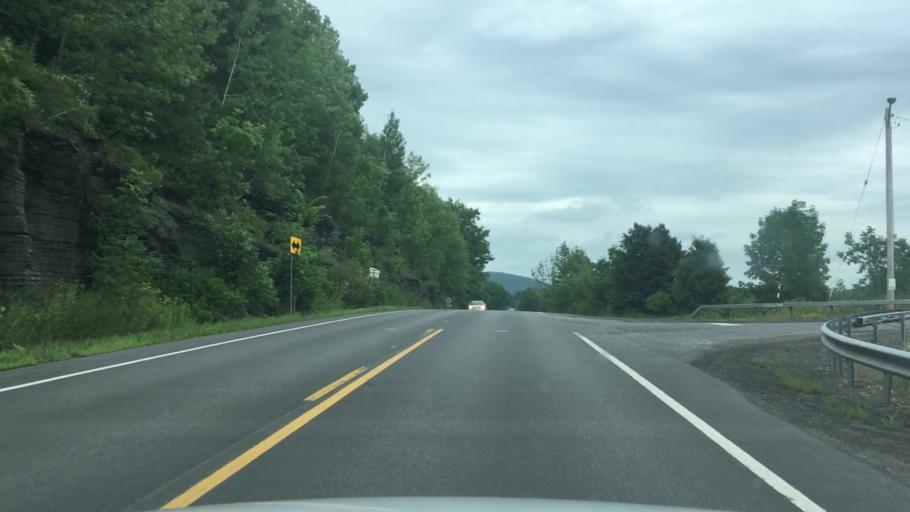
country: US
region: New York
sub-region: Otsego County
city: West End
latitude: 42.4345
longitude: -75.1236
